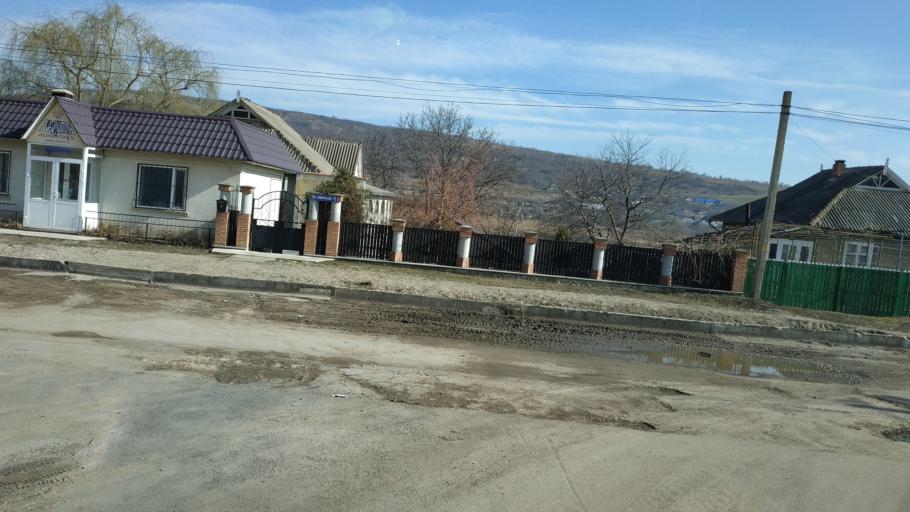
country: MD
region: Nisporeni
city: Nisporeni
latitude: 47.0681
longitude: 28.1737
